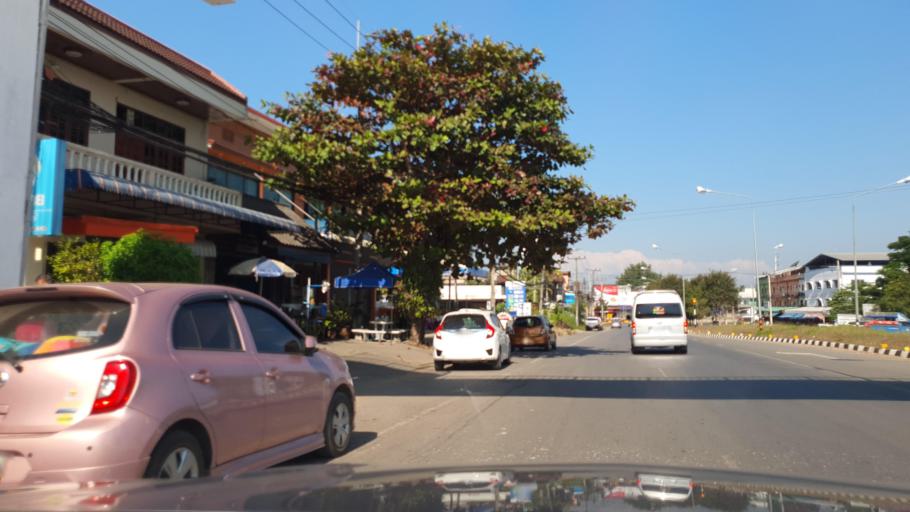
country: TH
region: Nan
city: Pua
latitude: 19.1761
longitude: 100.9162
